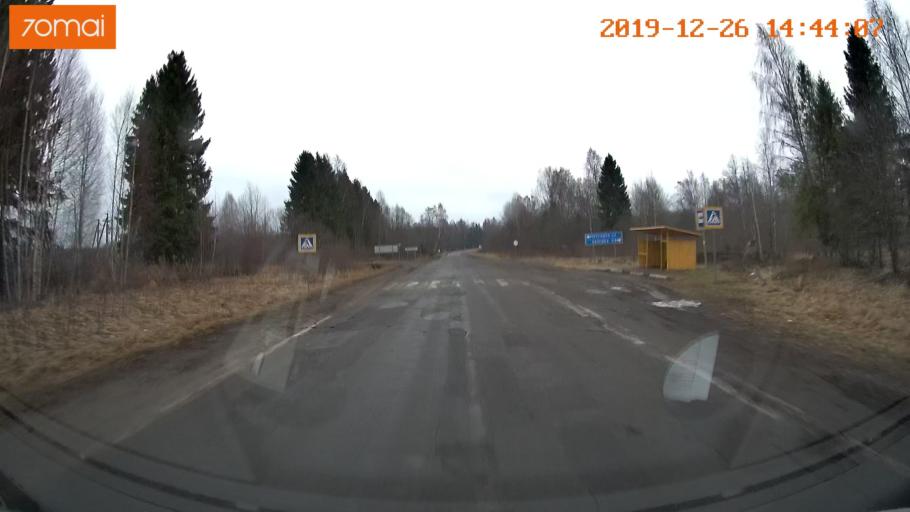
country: RU
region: Jaroslavl
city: Poshekhon'ye
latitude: 58.3508
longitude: 39.0475
